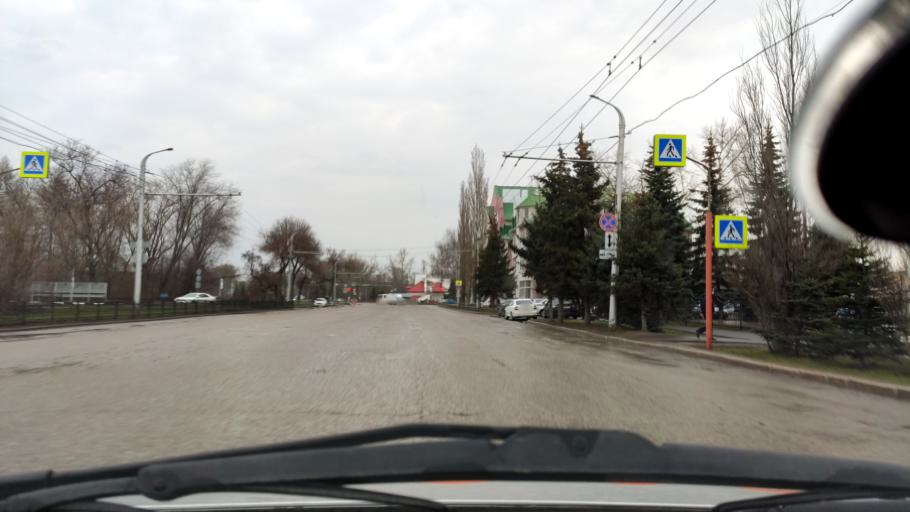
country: RU
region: Bashkortostan
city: Sterlitamak
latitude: 53.6528
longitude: 55.9476
